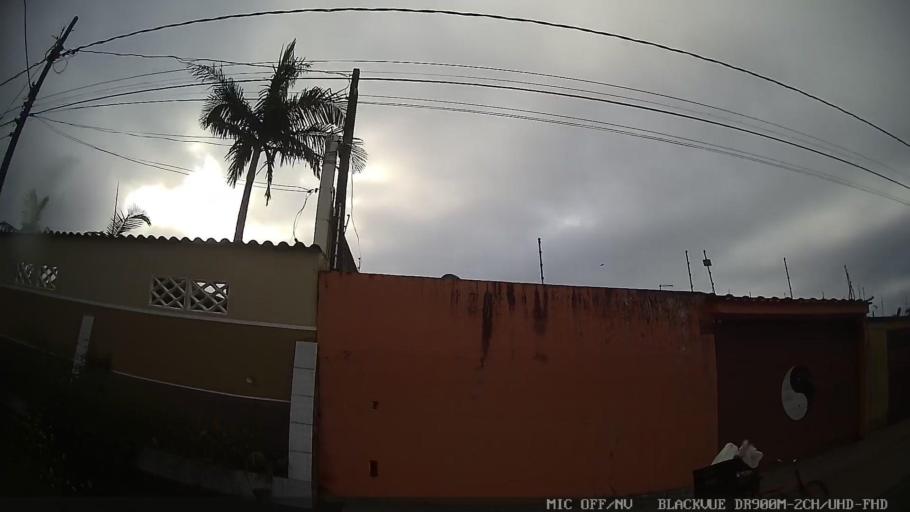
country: BR
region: Sao Paulo
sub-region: Itanhaem
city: Itanhaem
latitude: -24.1671
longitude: -46.7599
